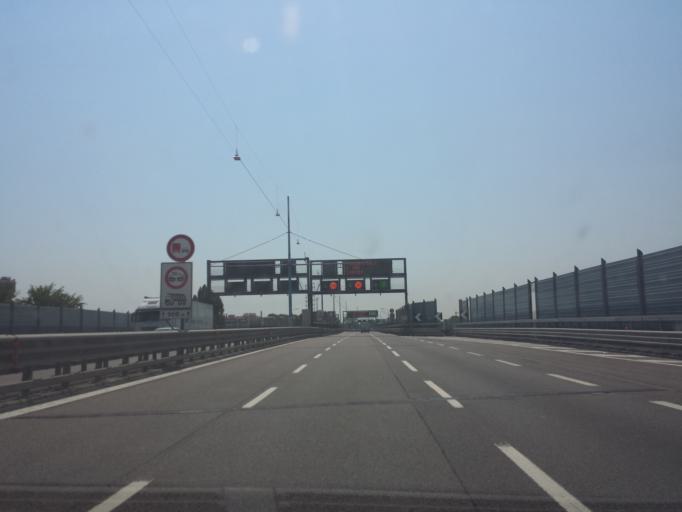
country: IT
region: Veneto
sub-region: Provincia di Venezia
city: Mestre
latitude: 45.4850
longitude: 12.2190
